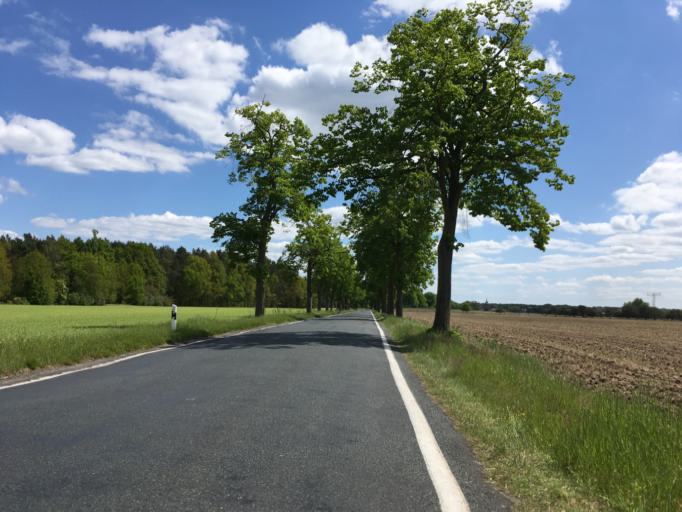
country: DE
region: Brandenburg
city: Wandlitz
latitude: 52.7835
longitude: 13.4228
